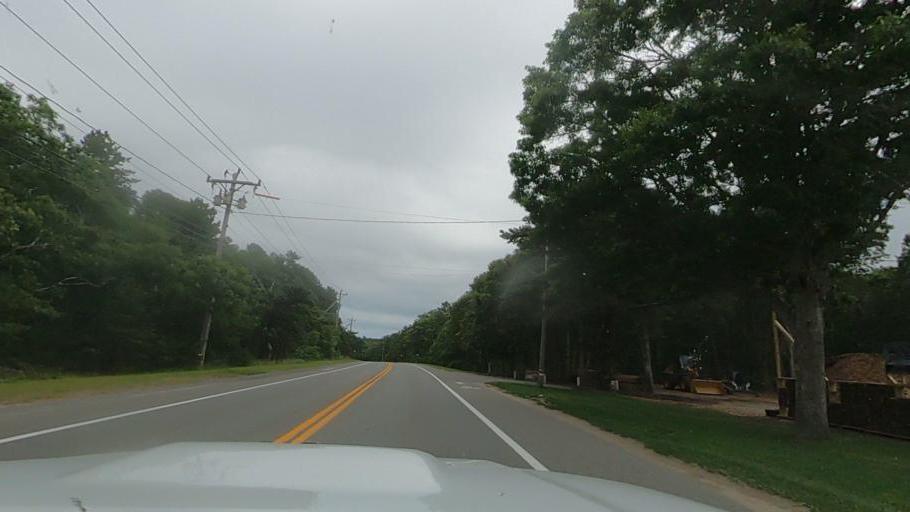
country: US
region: Massachusetts
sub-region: Barnstable County
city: Truro
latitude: 41.9806
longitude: -70.0426
